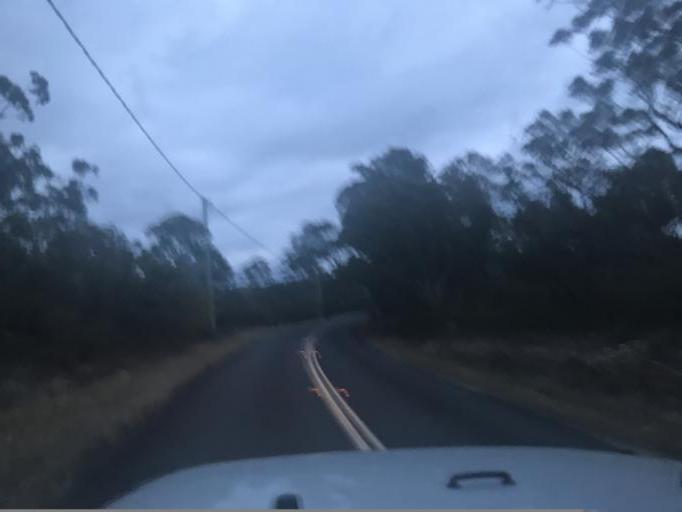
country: AU
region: New South Wales
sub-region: Hawkesbury
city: Pitt Town
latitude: -33.4672
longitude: 150.8506
